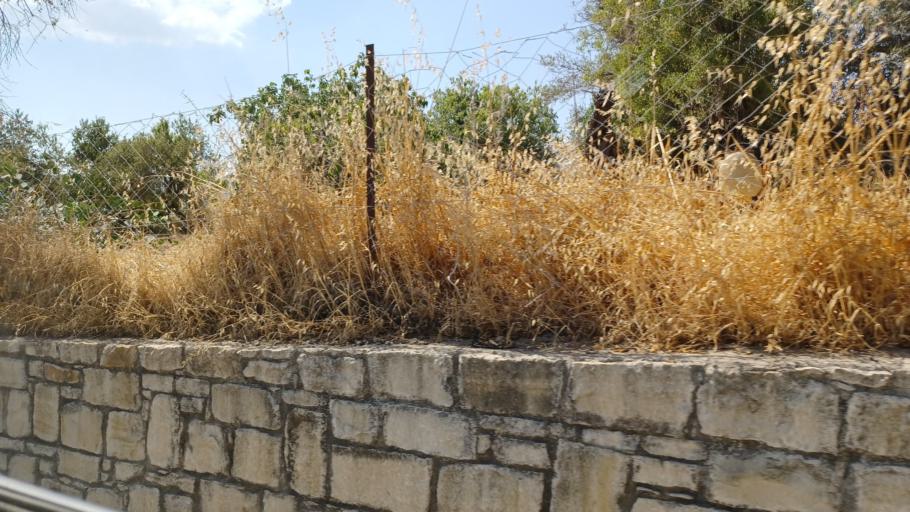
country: CY
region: Pafos
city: Tala
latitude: 34.9235
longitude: 32.4761
